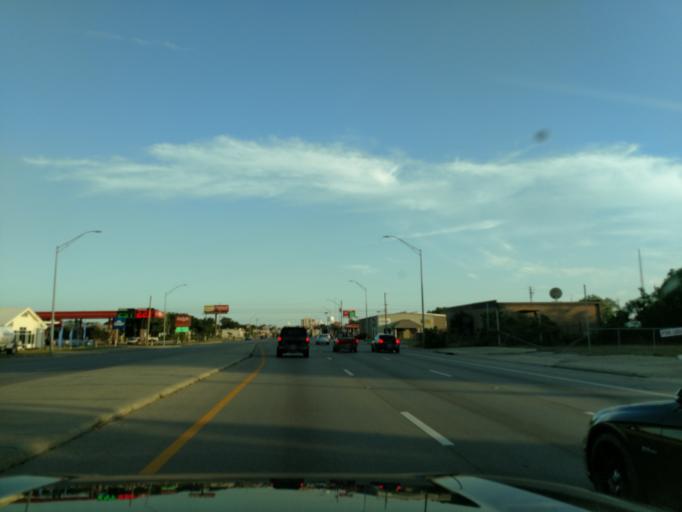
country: US
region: Mississippi
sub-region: Harrison County
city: West Gulfport
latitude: 30.3878
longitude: -89.0932
